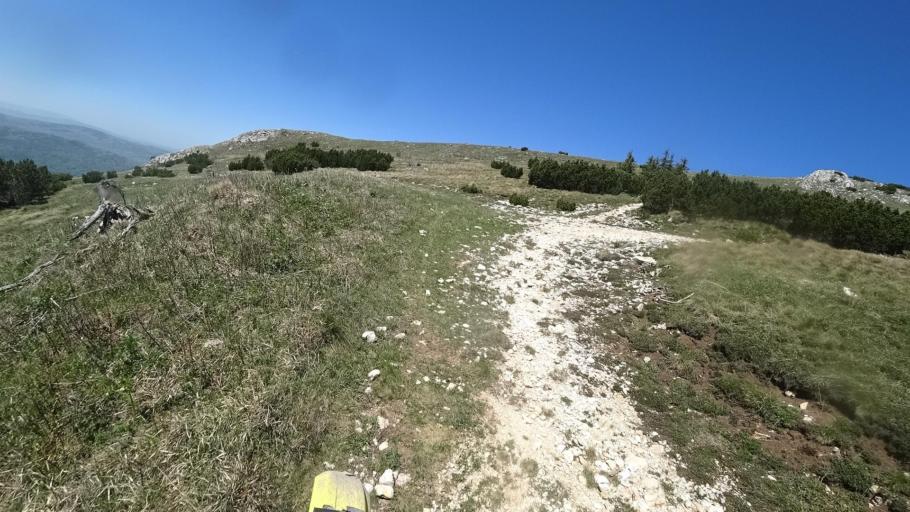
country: BA
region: Federation of Bosnia and Herzegovina
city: Rumboci
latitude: 43.8663
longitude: 17.4504
